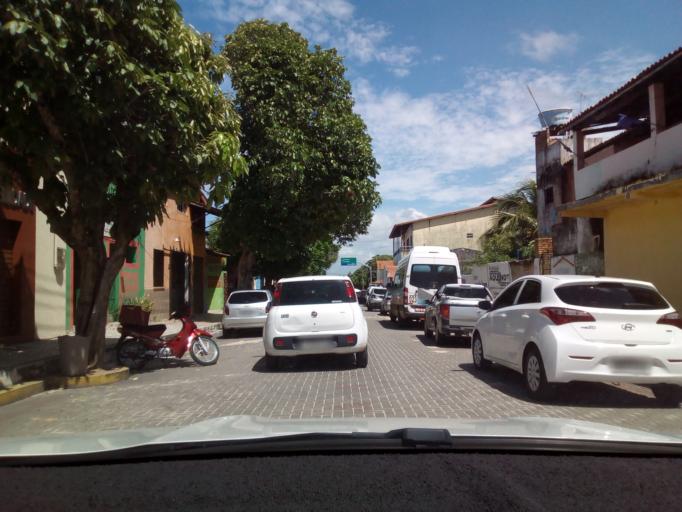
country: BR
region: Ceara
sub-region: Beberibe
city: Beberibe
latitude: -4.1819
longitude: -38.1307
